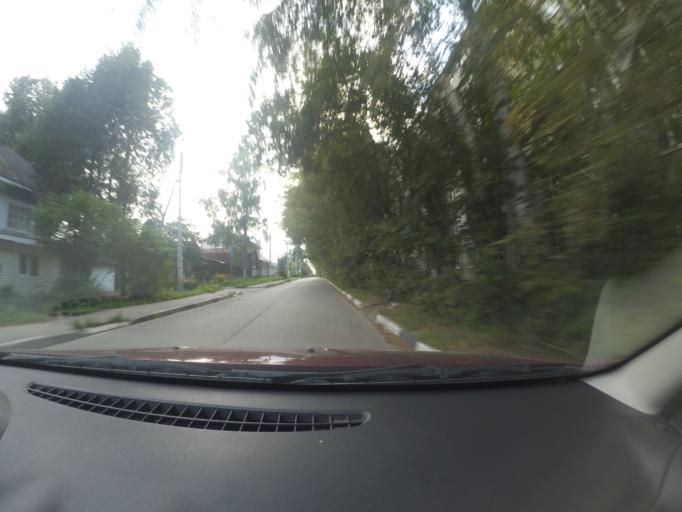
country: RU
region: Nizjnij Novgorod
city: Nizhniy Novgorod
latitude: 56.2933
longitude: 44.0294
